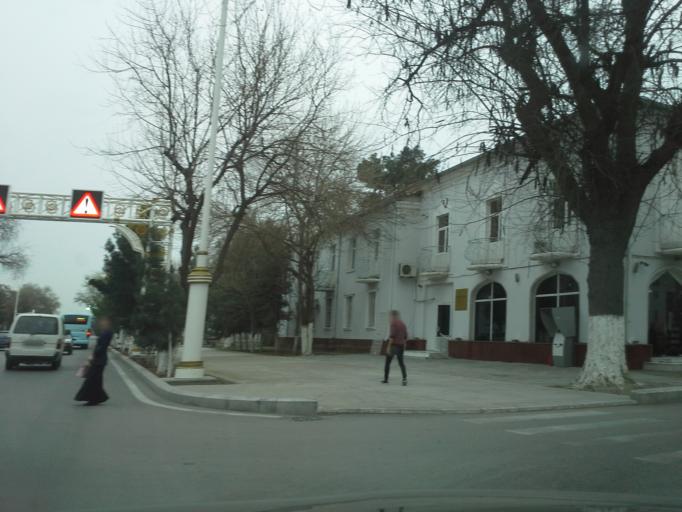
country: TM
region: Ahal
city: Ashgabat
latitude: 37.9566
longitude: 58.3605
